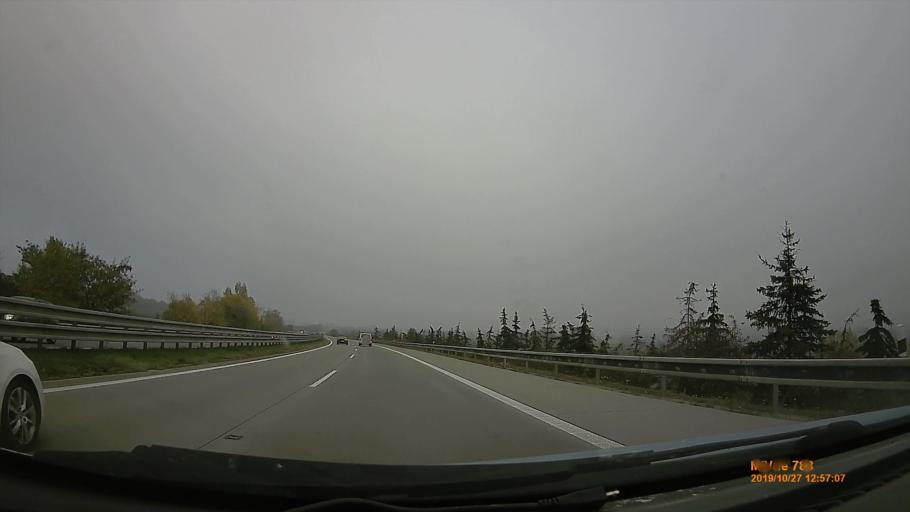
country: CZ
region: South Moravian
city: Vinicne Sumice
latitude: 49.1844
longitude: 16.8395
